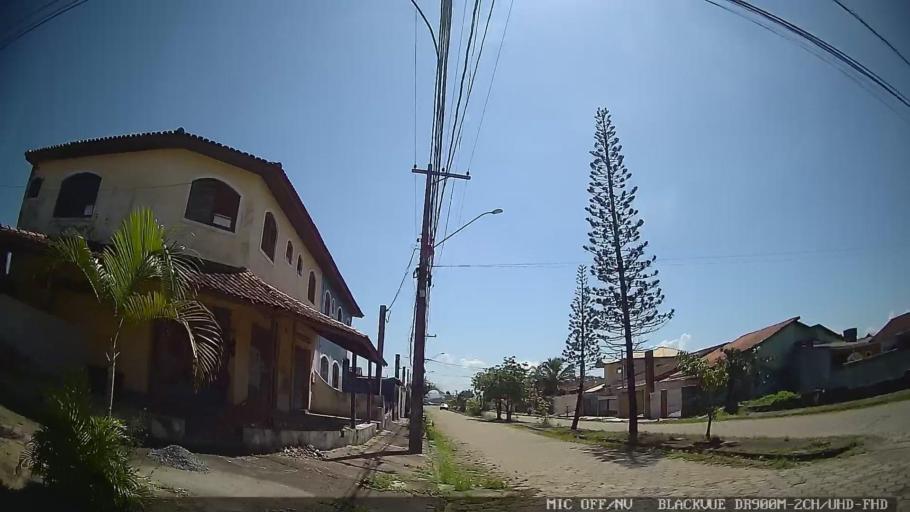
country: BR
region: Sao Paulo
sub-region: Peruibe
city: Peruibe
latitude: -24.2991
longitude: -46.9805
